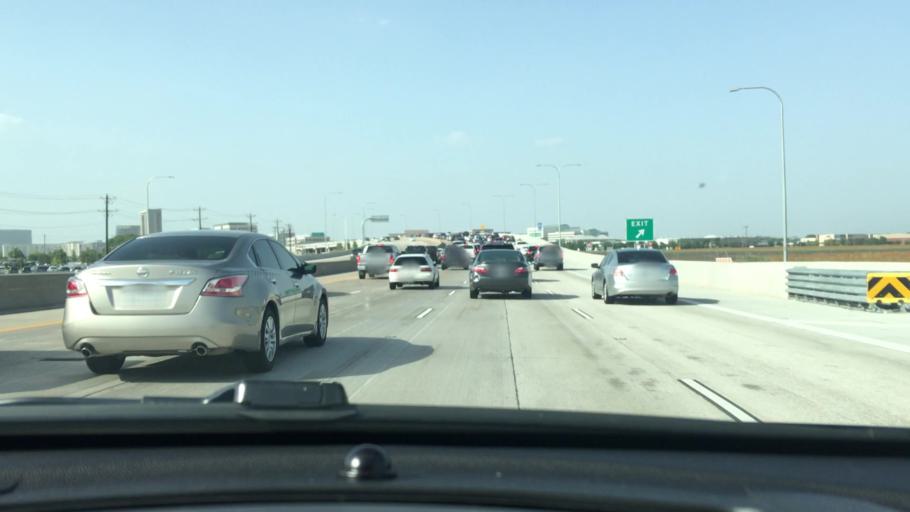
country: US
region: Texas
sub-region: Denton County
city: The Colony
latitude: 33.0606
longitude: -96.8268
